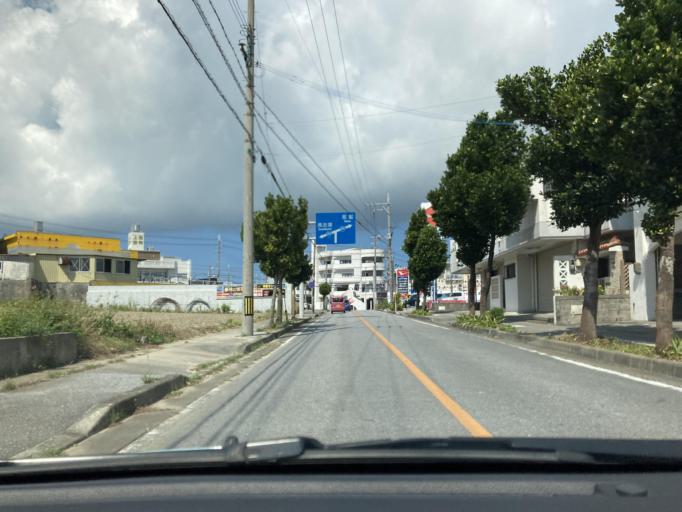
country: JP
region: Okinawa
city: Tomigusuku
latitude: 26.1754
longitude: 127.7198
